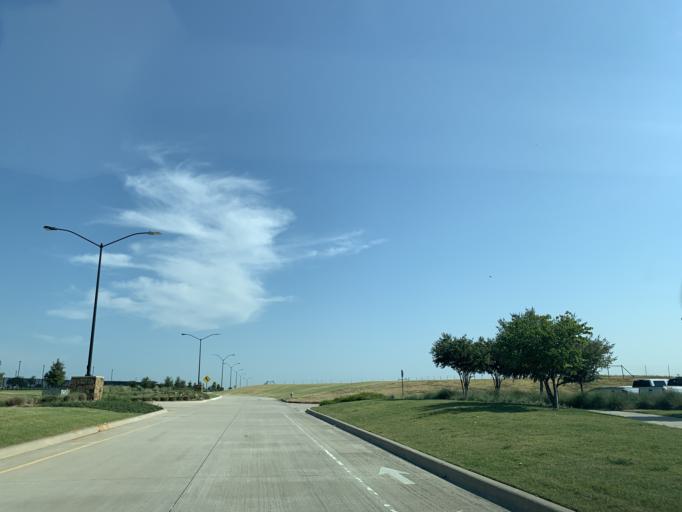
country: US
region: Texas
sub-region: Tarrant County
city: Keller
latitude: 32.9190
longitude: -97.3124
